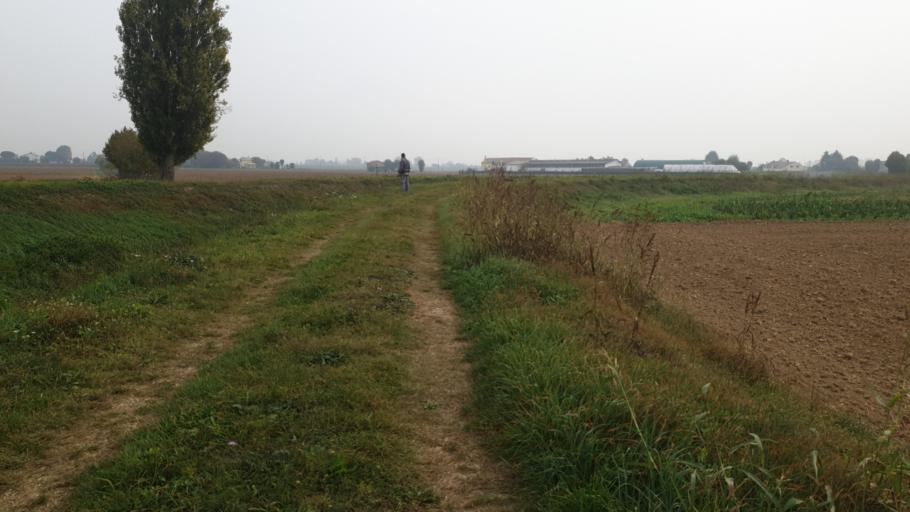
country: IT
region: Veneto
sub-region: Provincia di Padova
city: Casalserugo
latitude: 45.3339
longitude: 11.9259
